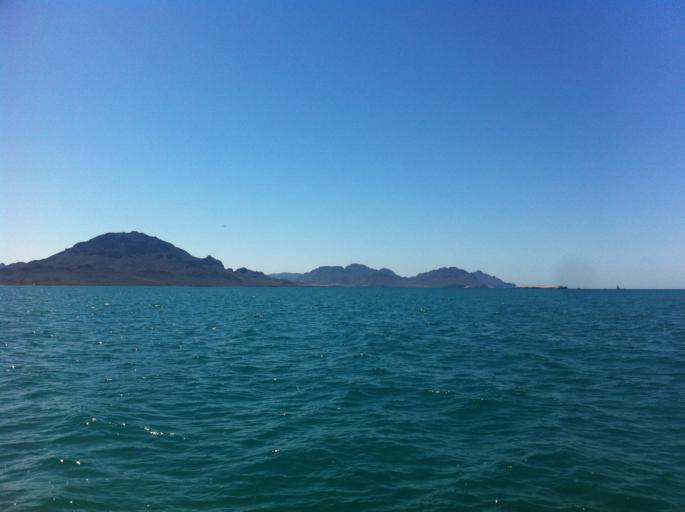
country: MX
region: Sonora
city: Heroica Guaymas
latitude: 27.9629
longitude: -111.0075
